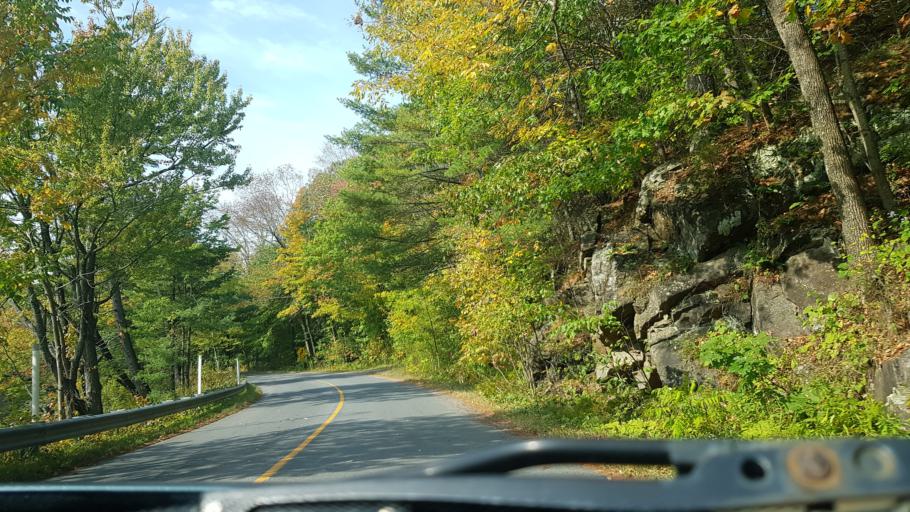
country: CA
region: Ontario
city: Gravenhurst
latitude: 44.7903
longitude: -79.2251
